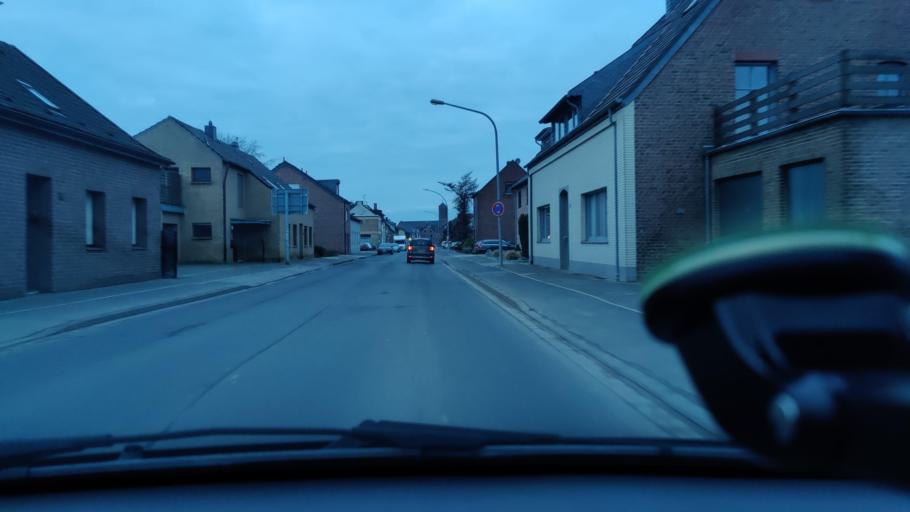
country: DE
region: North Rhine-Westphalia
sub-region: Regierungsbezirk Dusseldorf
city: Grefrath
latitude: 51.2965
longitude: 6.3631
